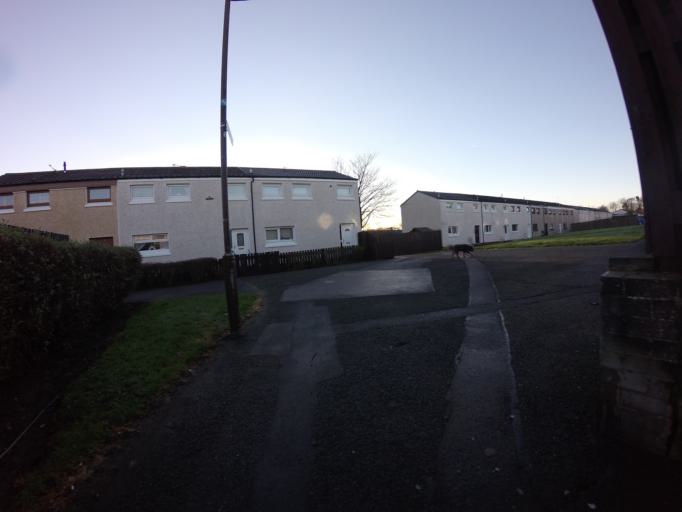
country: GB
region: Scotland
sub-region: West Lothian
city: Livingston
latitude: 55.8941
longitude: -3.5106
